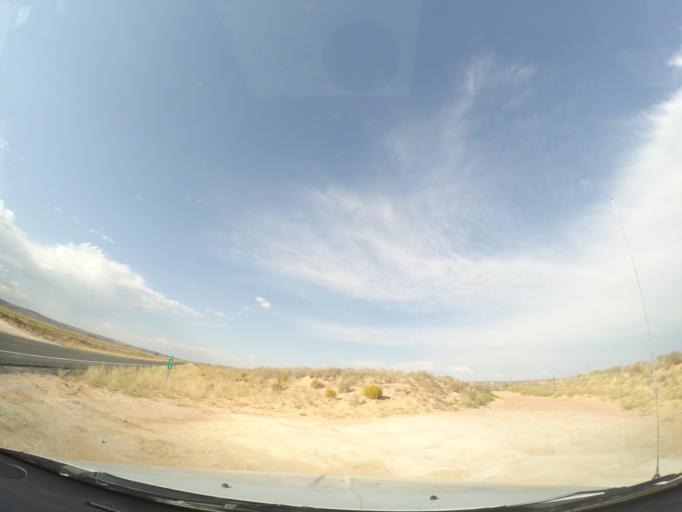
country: US
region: Arizona
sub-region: Coconino County
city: Tuba City
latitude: 36.4381
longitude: -111.4239
